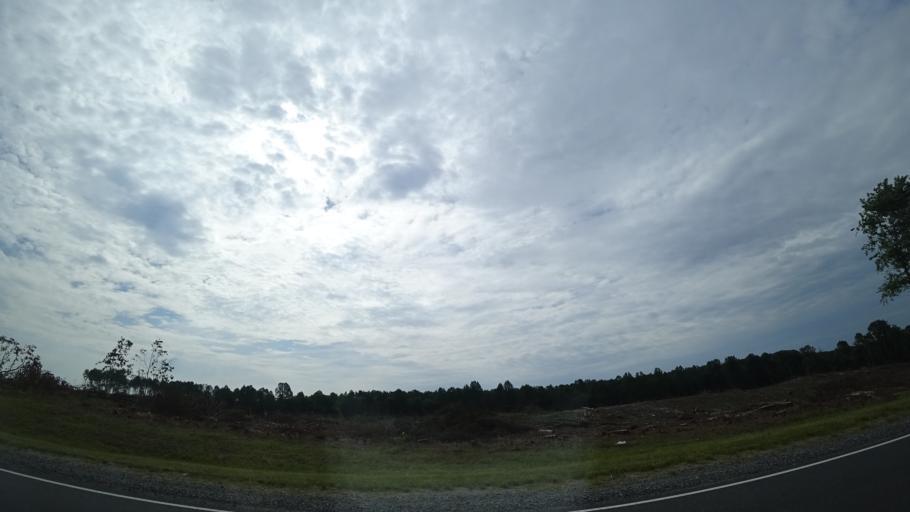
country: US
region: Virginia
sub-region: Spotsylvania County
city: Spotsylvania
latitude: 38.2276
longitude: -77.5637
